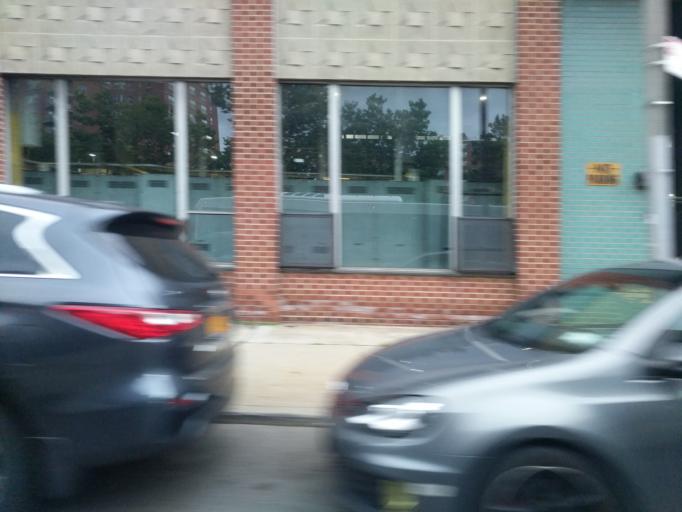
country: US
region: New York
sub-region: Queens County
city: Jamaica
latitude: 40.6769
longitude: -73.7688
